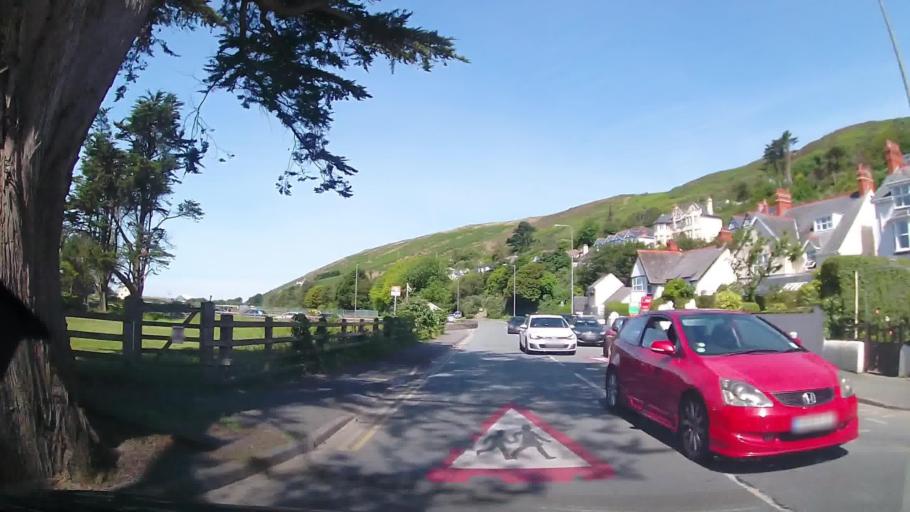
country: GB
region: Wales
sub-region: Gwynedd
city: Tywyn
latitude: 52.5447
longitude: -4.0527
